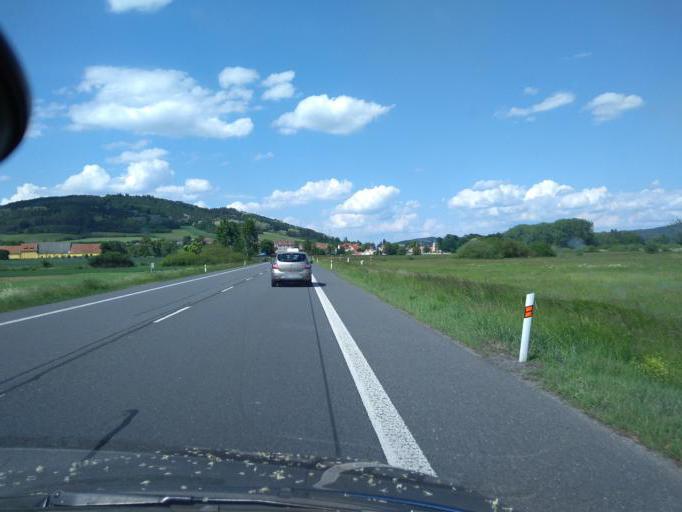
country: CZ
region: Plzensky
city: Svihov
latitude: 49.4976
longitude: 13.2913
